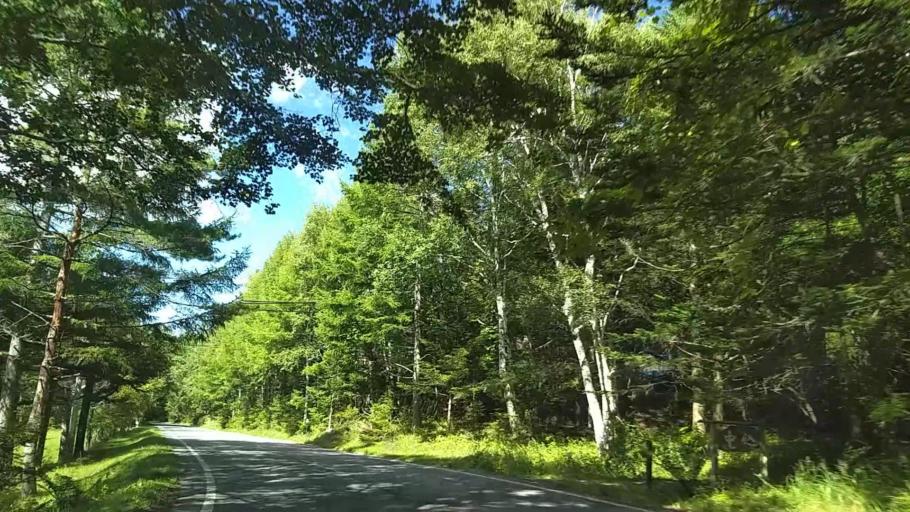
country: JP
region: Nagano
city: Chino
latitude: 36.1240
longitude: 138.2721
